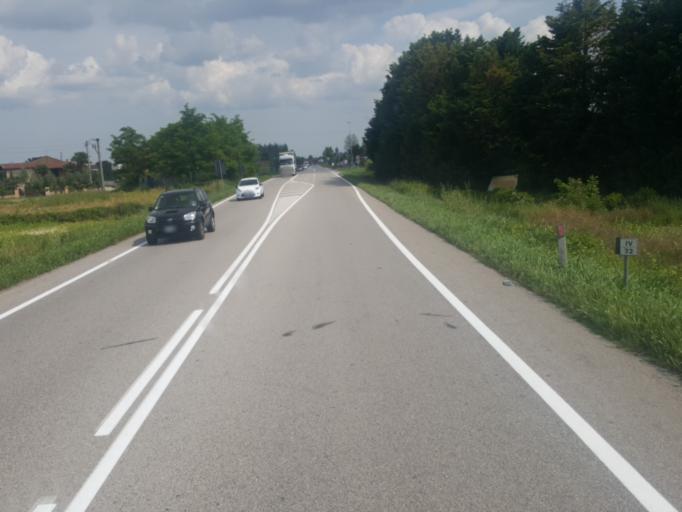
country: IT
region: Veneto
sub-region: Provincia di Padova
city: Vallonga
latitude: 45.2778
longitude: 12.0878
